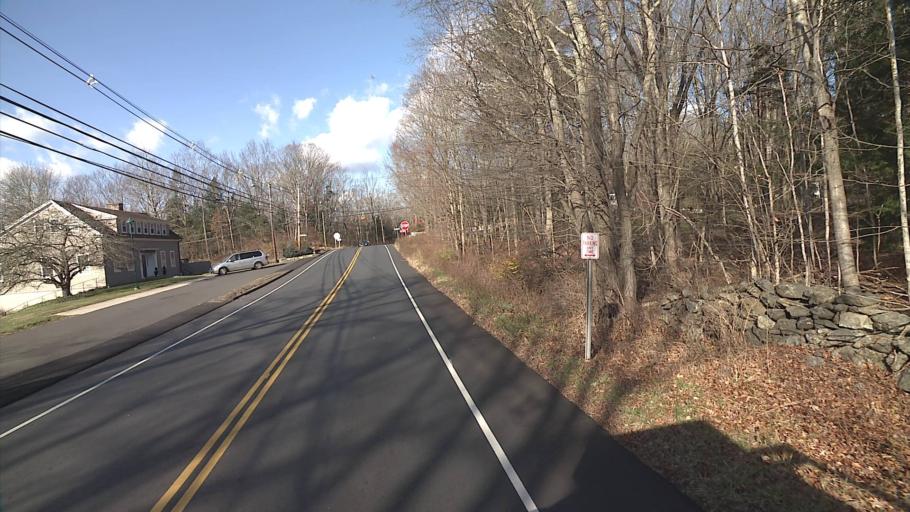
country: US
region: Connecticut
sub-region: Fairfield County
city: Georgetown
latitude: 41.2995
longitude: -73.4002
